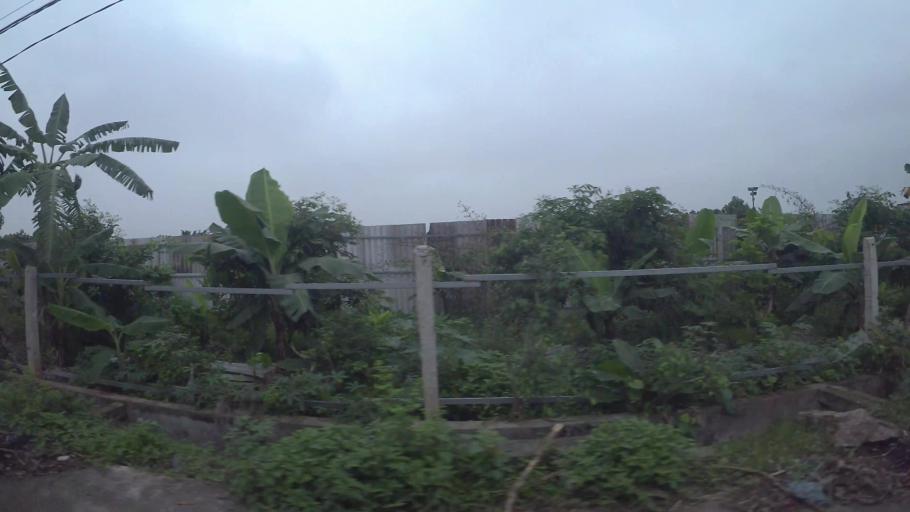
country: VN
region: Hung Yen
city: Van Giang
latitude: 20.9751
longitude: 105.8910
